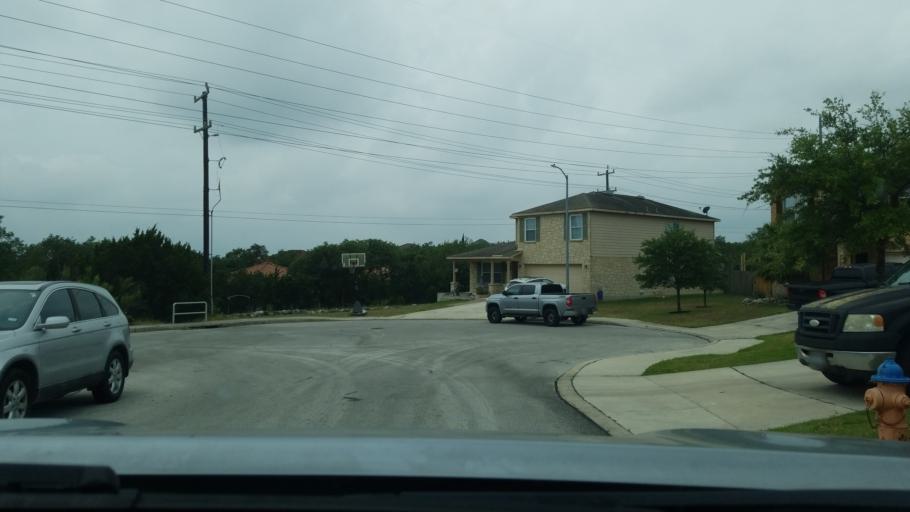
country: US
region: Texas
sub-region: Bexar County
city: Timberwood Park
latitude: 29.6802
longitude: -98.4655
